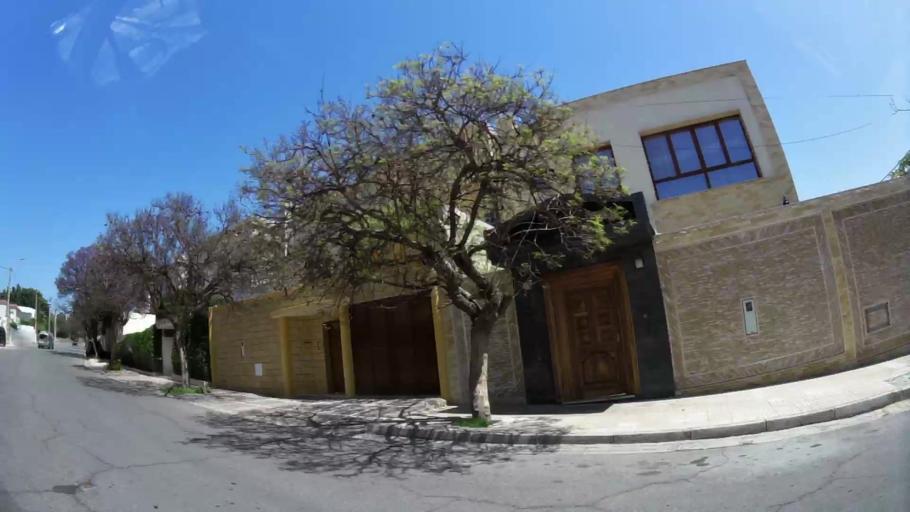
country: MA
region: Souss-Massa-Draa
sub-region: Agadir-Ida-ou-Tnan
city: Agadir
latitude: 30.4258
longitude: -9.5990
